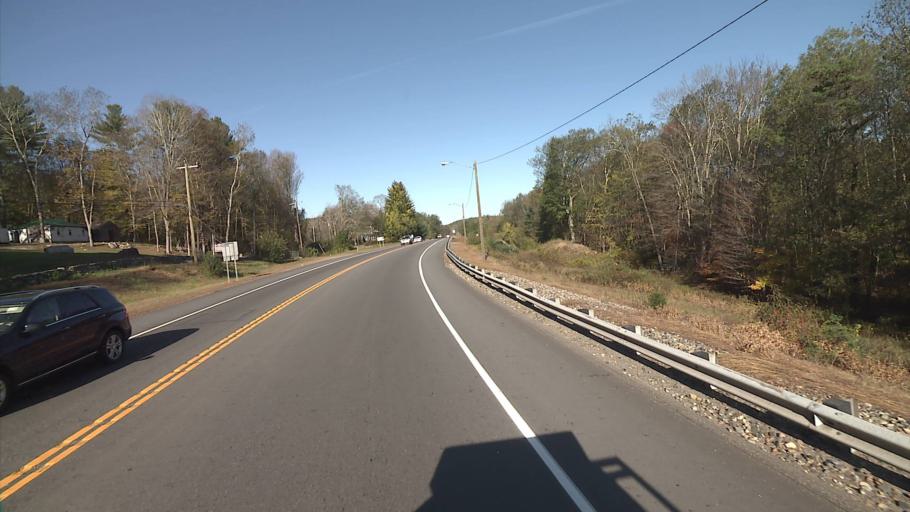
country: US
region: Connecticut
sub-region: Tolland County
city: Coventry Lake
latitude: 41.7282
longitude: -72.3511
